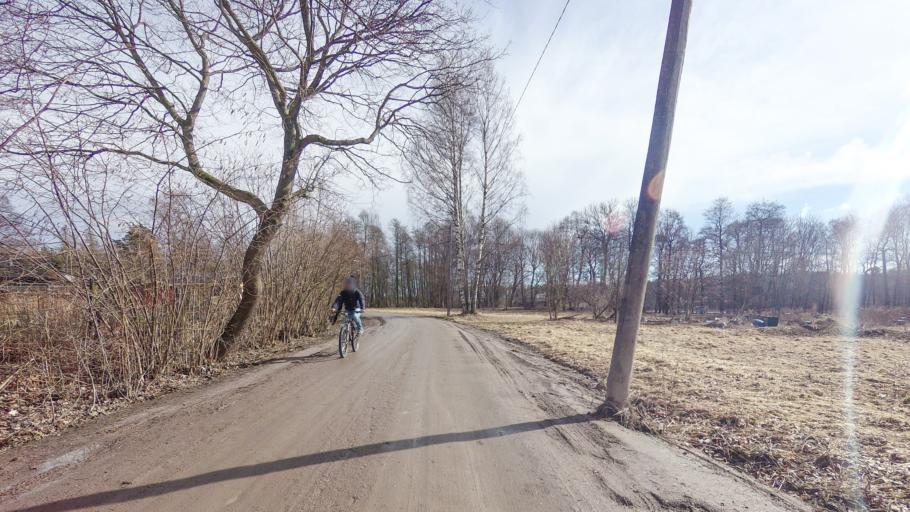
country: FI
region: Uusimaa
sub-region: Helsinki
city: Helsinki
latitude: 60.1925
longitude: 25.0169
